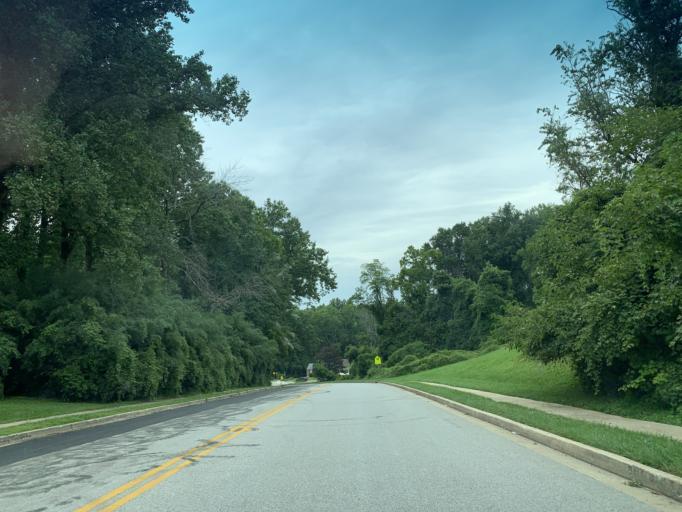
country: US
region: Maryland
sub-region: Baltimore County
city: Carney
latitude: 39.4126
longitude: -76.5297
